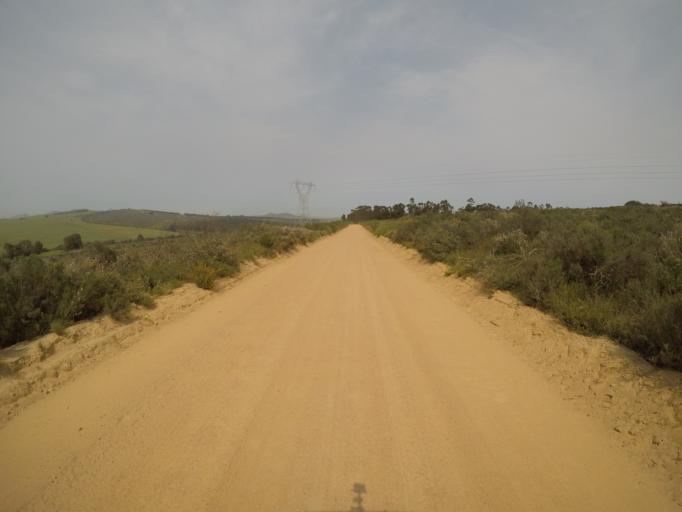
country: ZA
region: Western Cape
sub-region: West Coast District Municipality
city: Malmesbury
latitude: -33.4526
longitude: 18.7437
